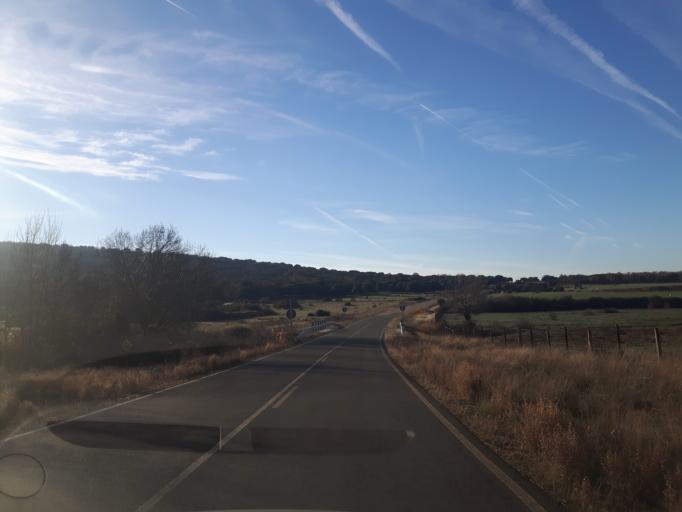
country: ES
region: Castille and Leon
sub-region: Provincia de Salamanca
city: Olmedo de Camaces
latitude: 40.9060
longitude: -6.6183
